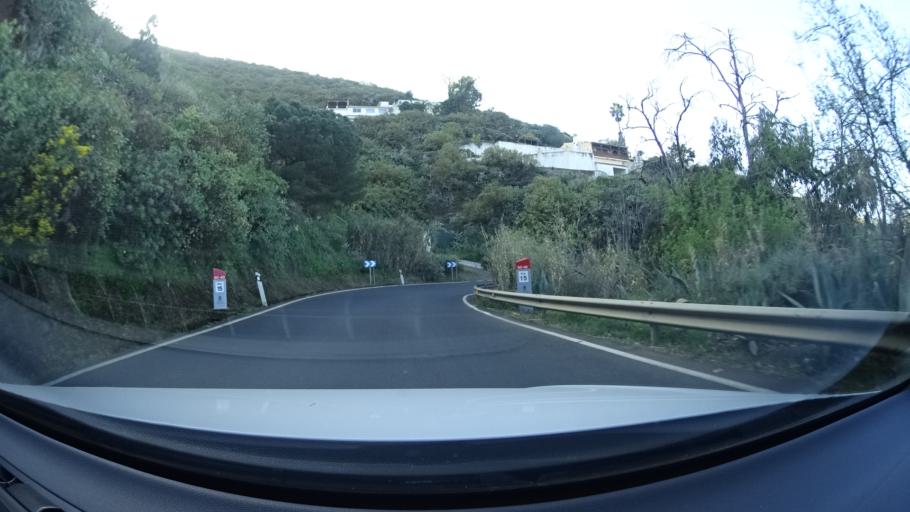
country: ES
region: Canary Islands
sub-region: Provincia de Las Palmas
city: Vega de San Mateo
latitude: 28.0122
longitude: -15.5360
